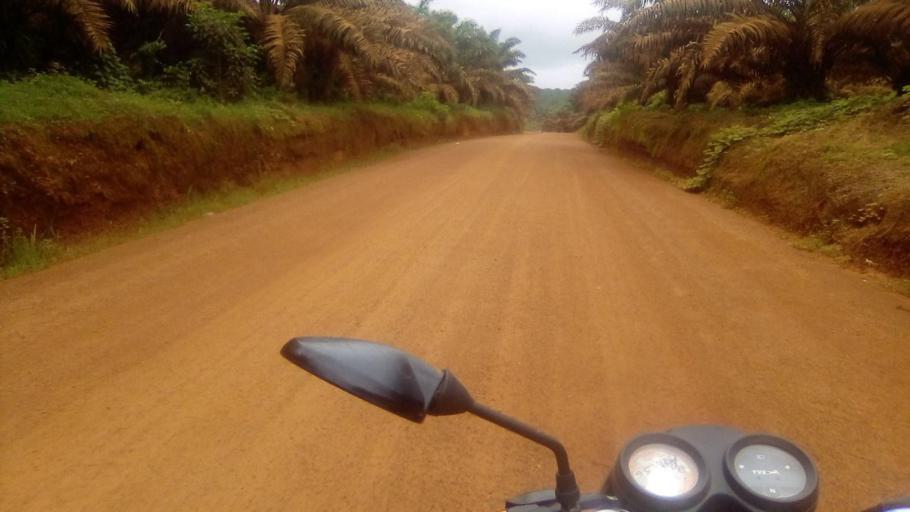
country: SL
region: Southern Province
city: Tongole
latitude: 7.4326
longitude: -11.8506
